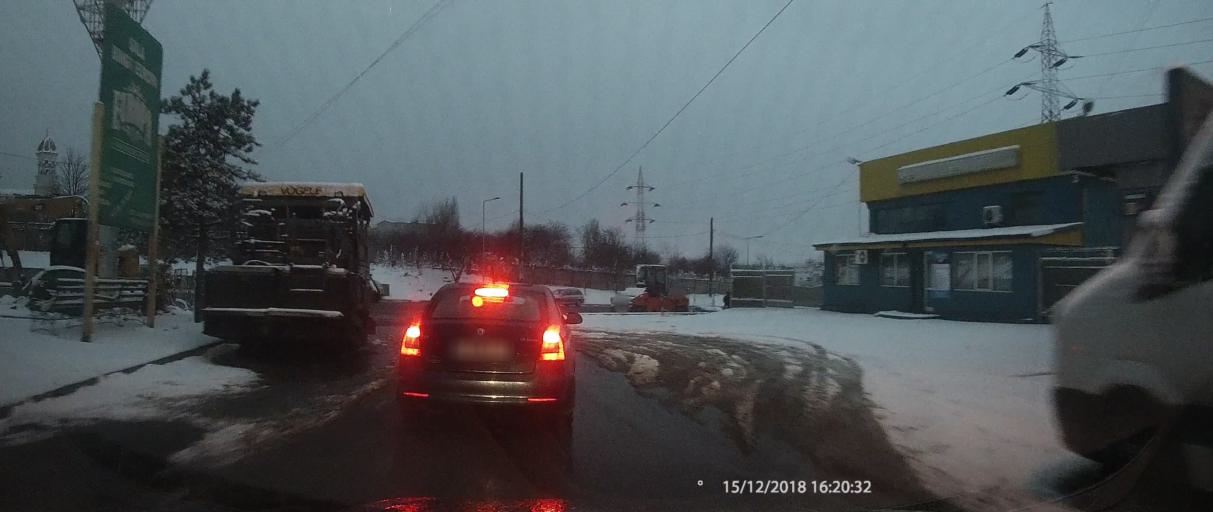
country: RO
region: Galati
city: Galati
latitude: 45.4137
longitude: 28.0050
